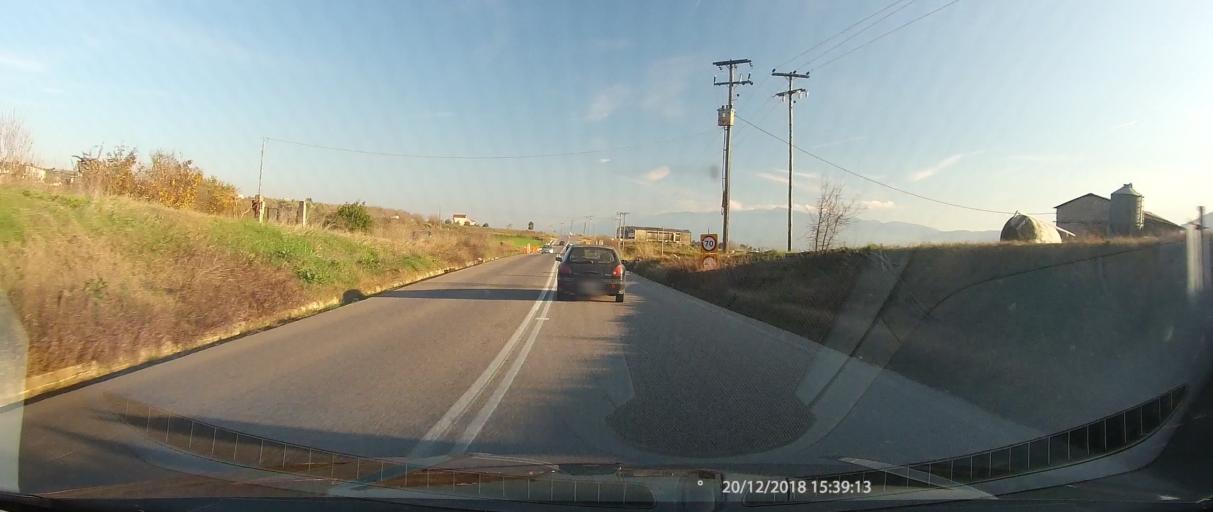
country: GR
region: Central Greece
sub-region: Nomos Fthiotidos
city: Stavros
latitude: 38.8982
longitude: 22.3614
